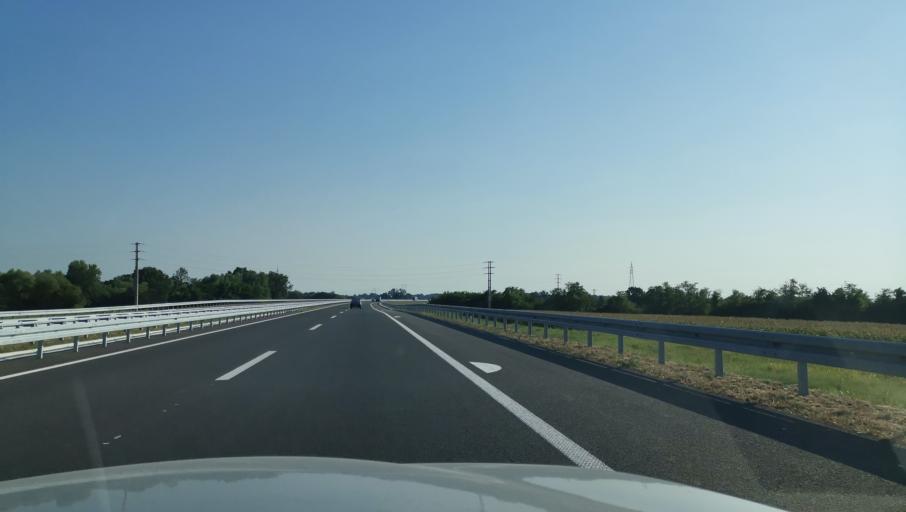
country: RS
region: Central Serbia
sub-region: Belgrade
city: Obrenovac
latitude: 44.6345
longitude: 20.2034
